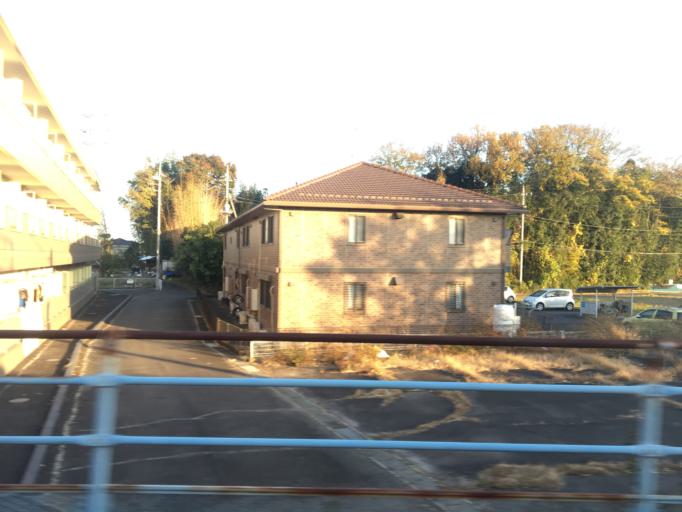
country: JP
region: Gunma
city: Takasaki
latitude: 36.3576
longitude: 139.0234
